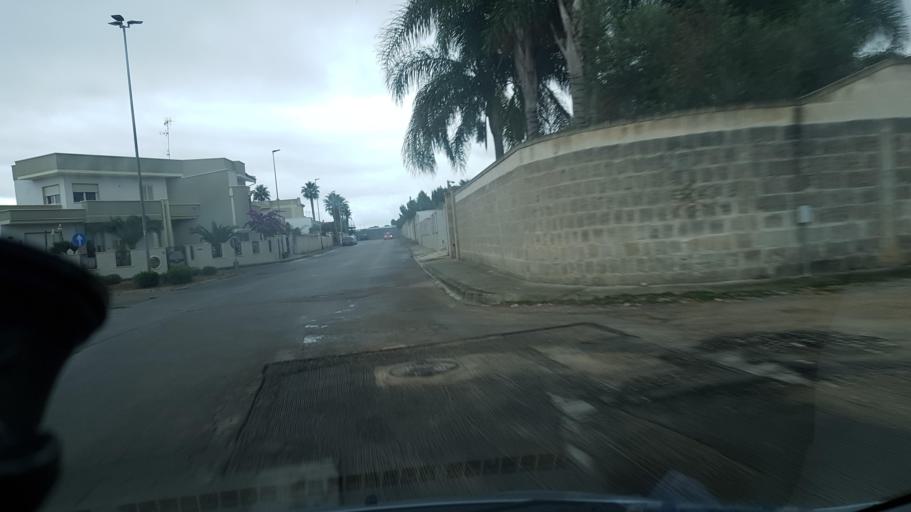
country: IT
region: Apulia
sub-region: Provincia di Lecce
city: Carmiano
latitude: 40.3423
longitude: 18.0375
